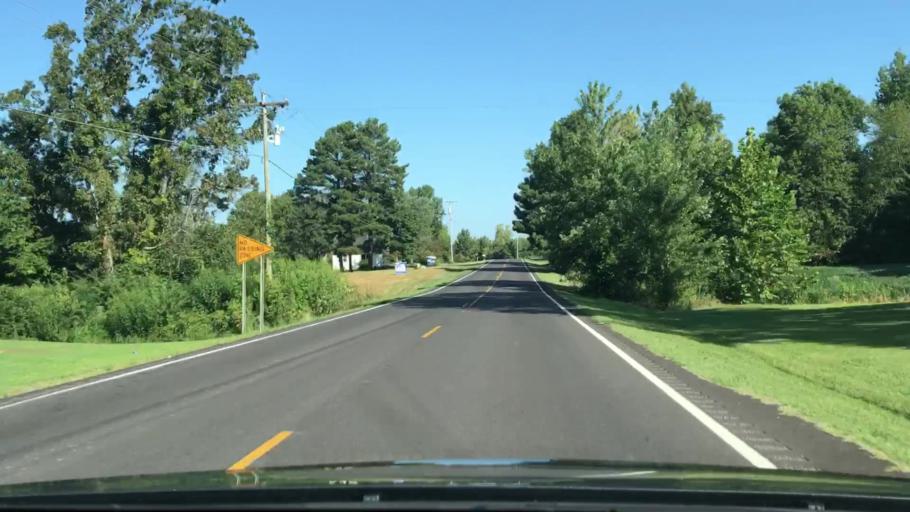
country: US
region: Kentucky
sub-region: Marshall County
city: Benton
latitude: 36.7731
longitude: -88.4415
